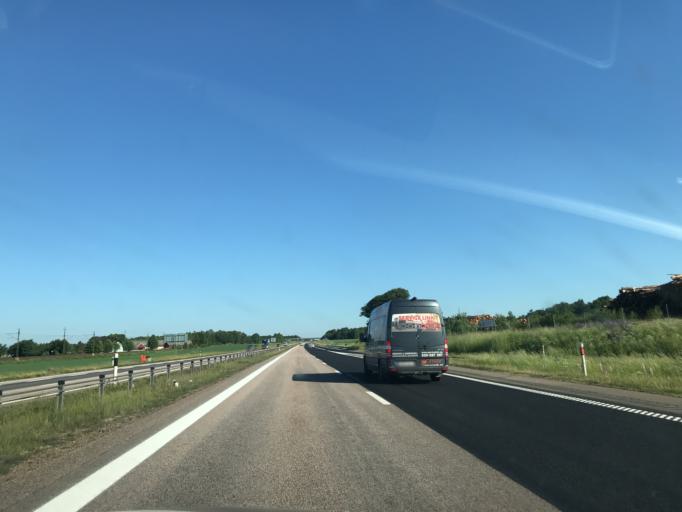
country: SE
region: Halland
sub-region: Varbergs Kommun
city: Tvaaker
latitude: 56.9817
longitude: 12.4246
